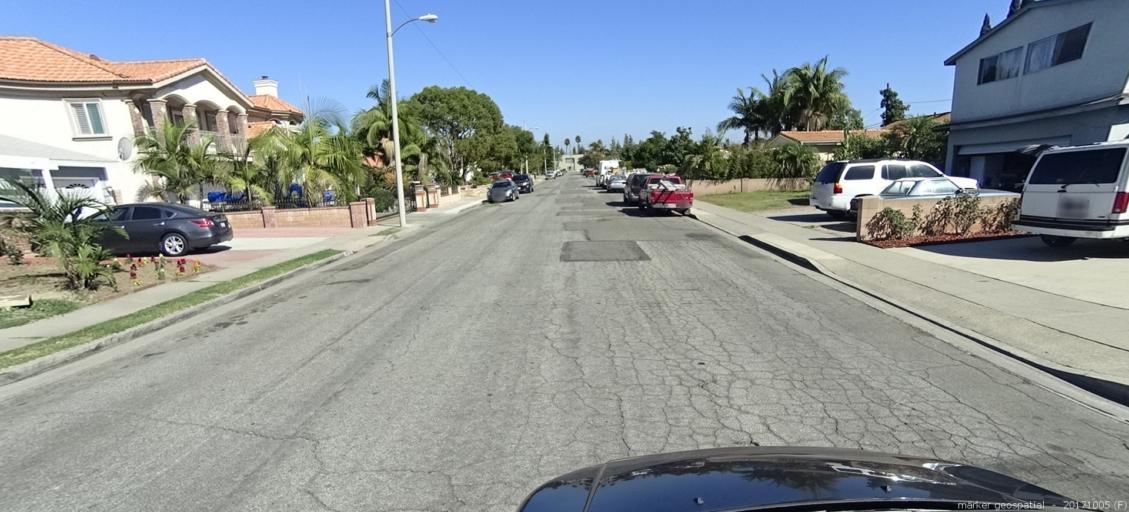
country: US
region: California
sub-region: Orange County
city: Garden Grove
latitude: 33.7806
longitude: -117.9487
